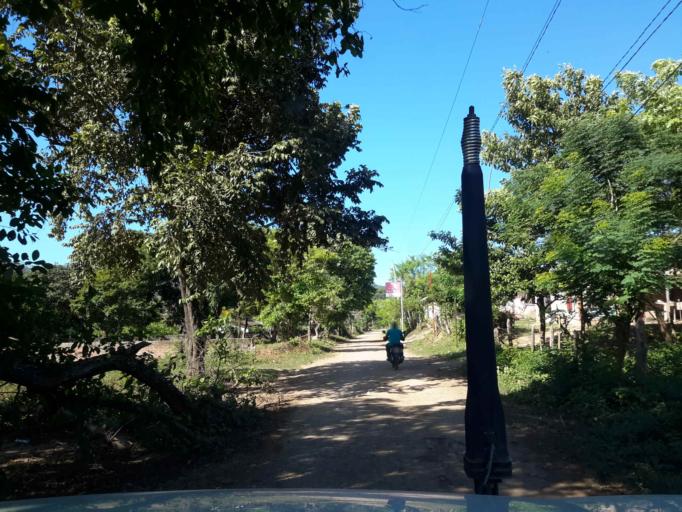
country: NI
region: Rivas
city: Tola
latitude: 11.4630
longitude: -85.9466
